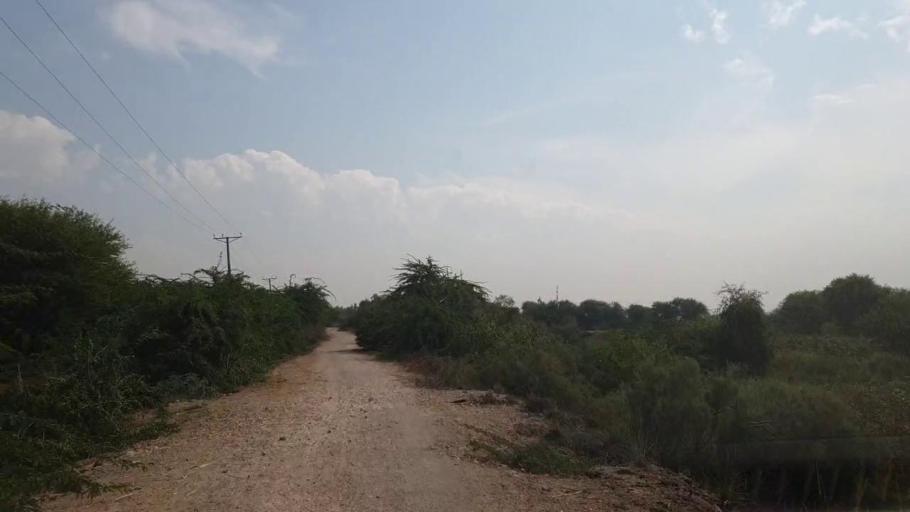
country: PK
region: Sindh
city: Tando Bago
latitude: 24.9317
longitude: 69.0063
